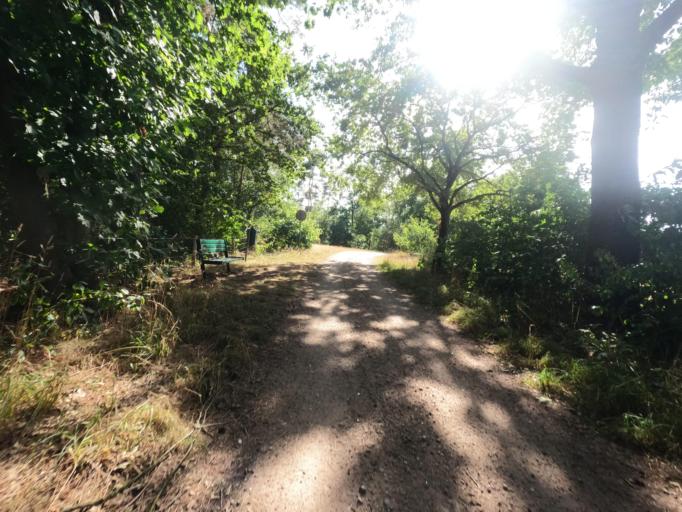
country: NL
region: Limburg
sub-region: Gemeente Beesel
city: Reuver
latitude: 51.2428
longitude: 6.0732
